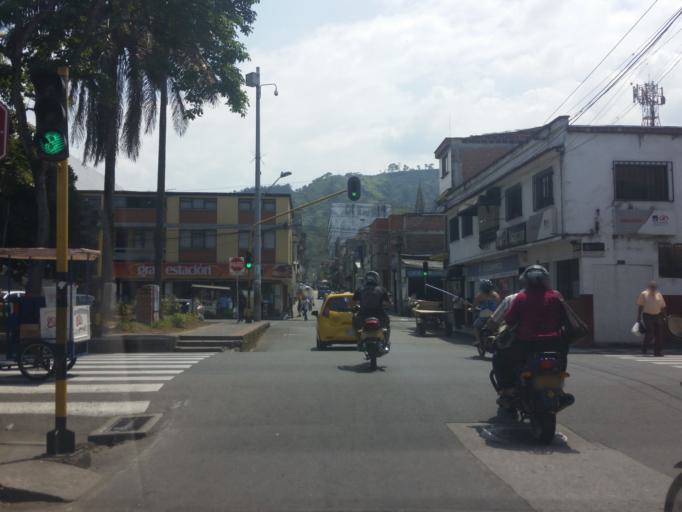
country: CO
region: Caldas
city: Chinchina
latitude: 4.9842
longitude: -75.6076
